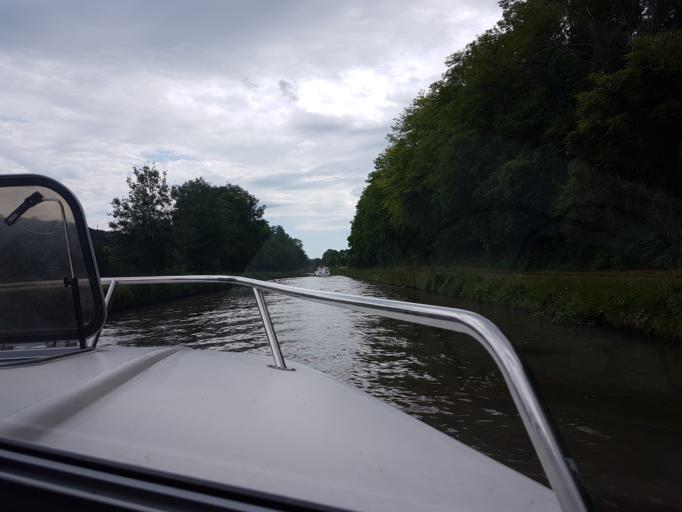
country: FR
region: Bourgogne
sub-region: Departement de la Nievre
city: Clamecy
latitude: 47.4862
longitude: 3.5243
